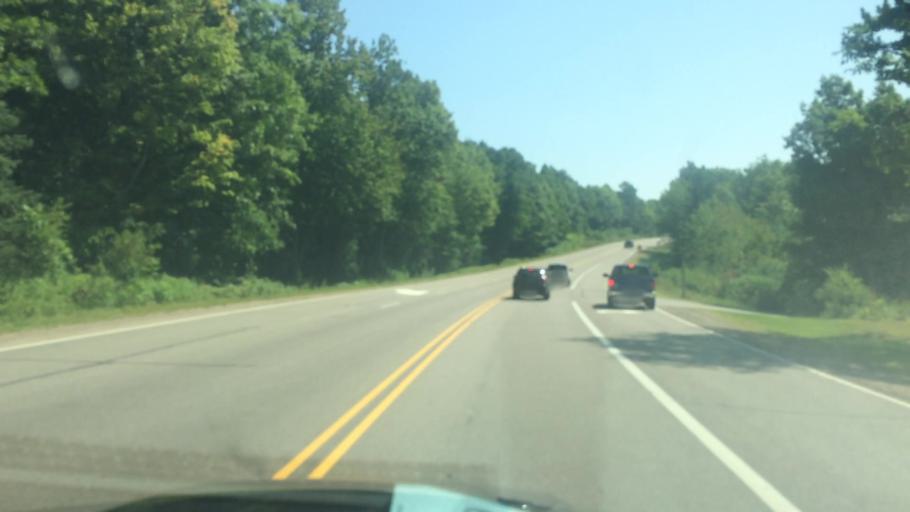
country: US
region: Wisconsin
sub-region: Oneida County
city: Rhinelander
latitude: 45.6173
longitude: -89.5249
